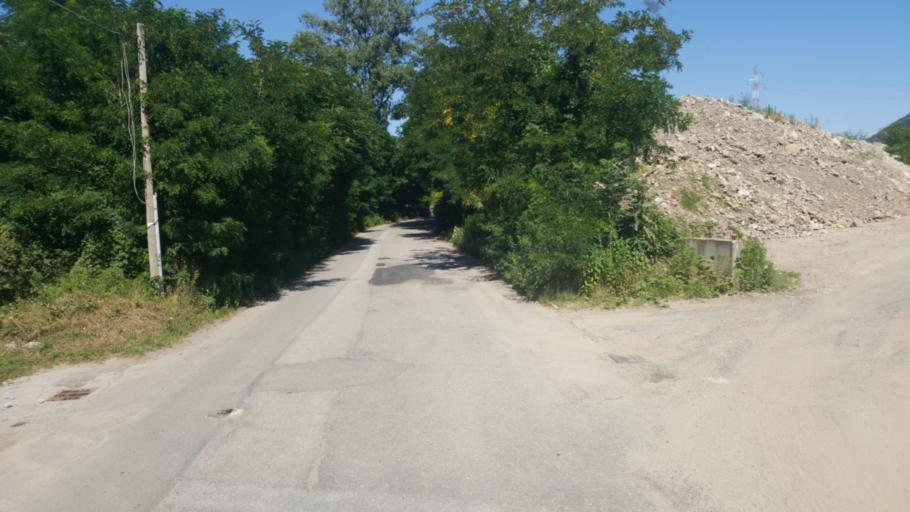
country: IT
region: Piedmont
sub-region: Provincia Verbano-Cusio-Ossola
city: Gravellona Toce
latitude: 45.9326
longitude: 8.4511
